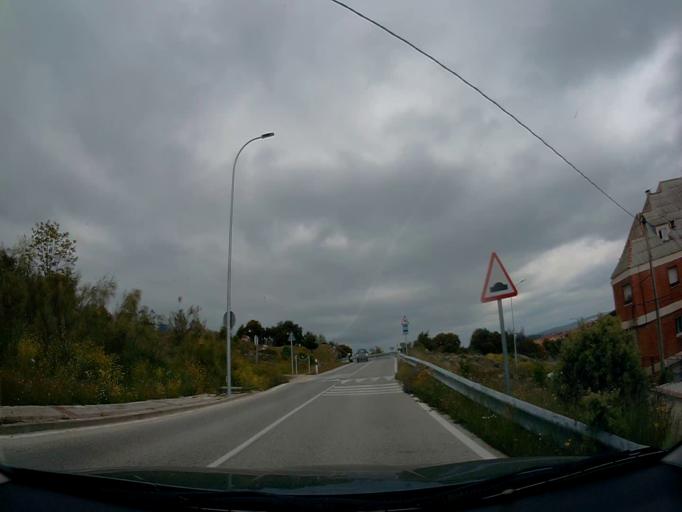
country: ES
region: Madrid
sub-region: Provincia de Madrid
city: Navalagamella
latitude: 40.4692
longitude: -4.1271
